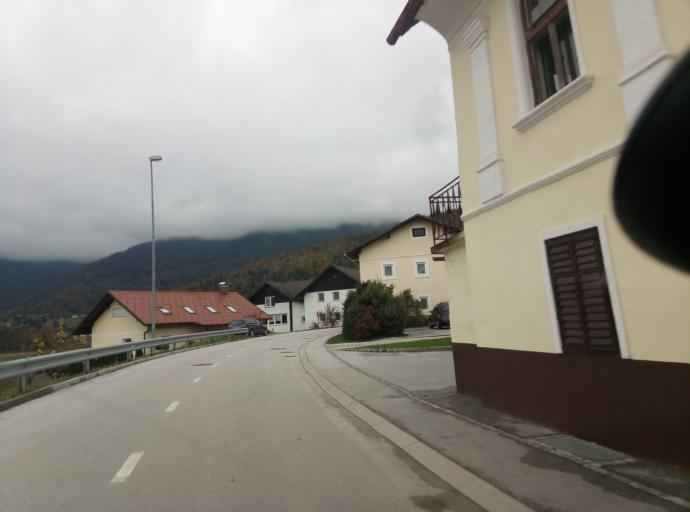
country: SI
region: Preddvor
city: Preddvor
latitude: 46.2910
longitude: 14.4270
